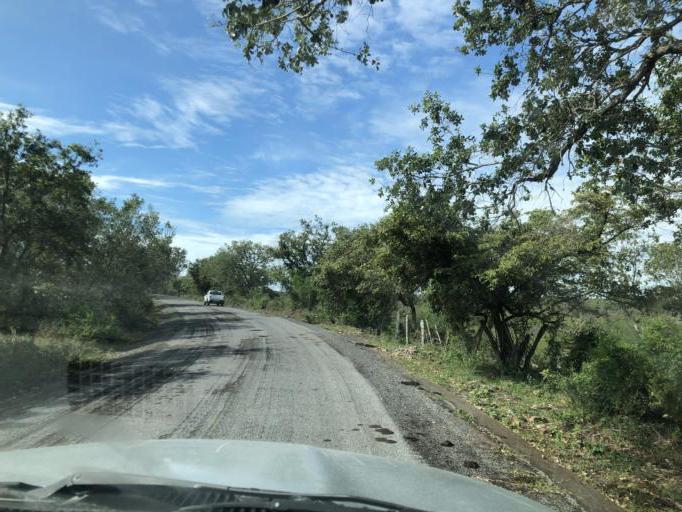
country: MX
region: Veracruz
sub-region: Alto Lucero de Gutierrez Barrios
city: Palma Sola
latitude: 19.7910
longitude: -96.5527
